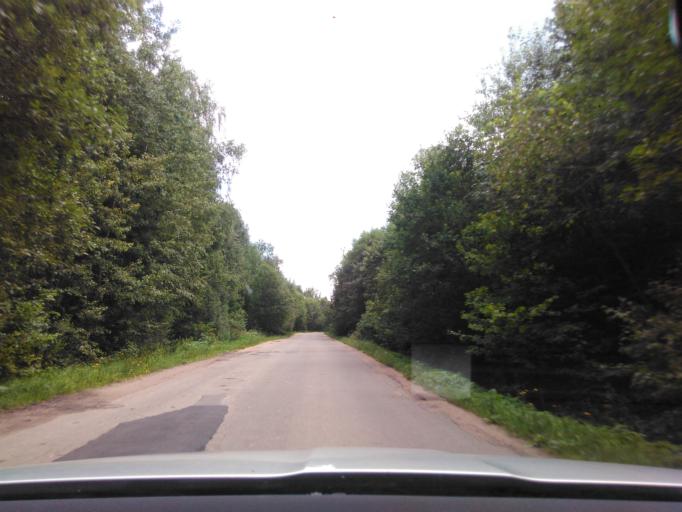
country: RU
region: Moskovskaya
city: Mendeleyevo
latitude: 56.1036
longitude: 37.2684
